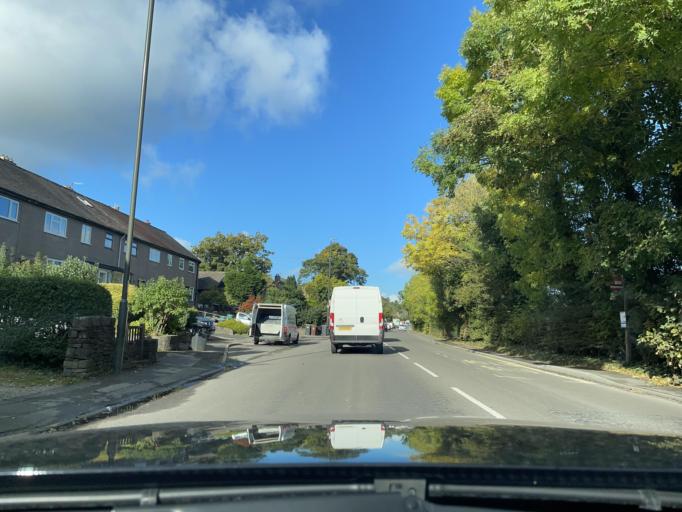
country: GB
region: England
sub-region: Derbyshire
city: New Mills
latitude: 53.3510
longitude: -1.9940
